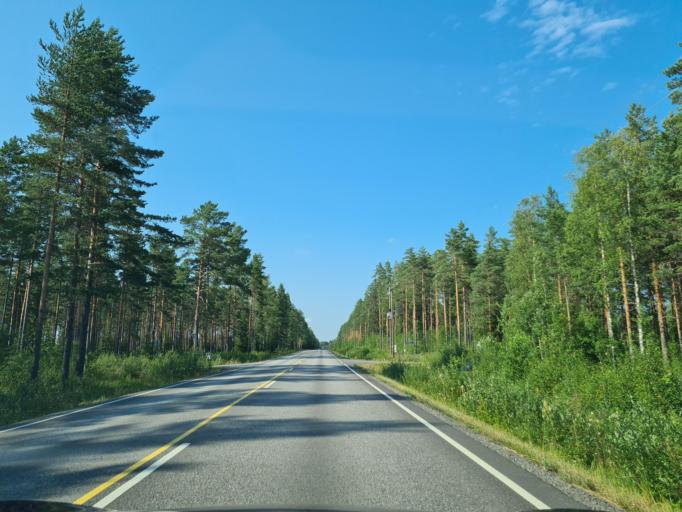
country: FI
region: Satakunta
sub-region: Pohjois-Satakunta
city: Kankaanpaeae
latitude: 61.9234
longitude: 22.5077
